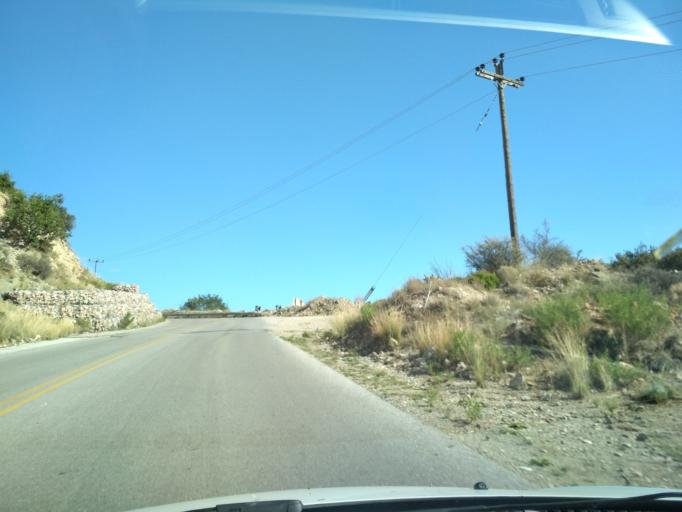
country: GR
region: Central Greece
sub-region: Nomos Evvoias
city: Roviai
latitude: 38.8525
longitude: 23.1408
